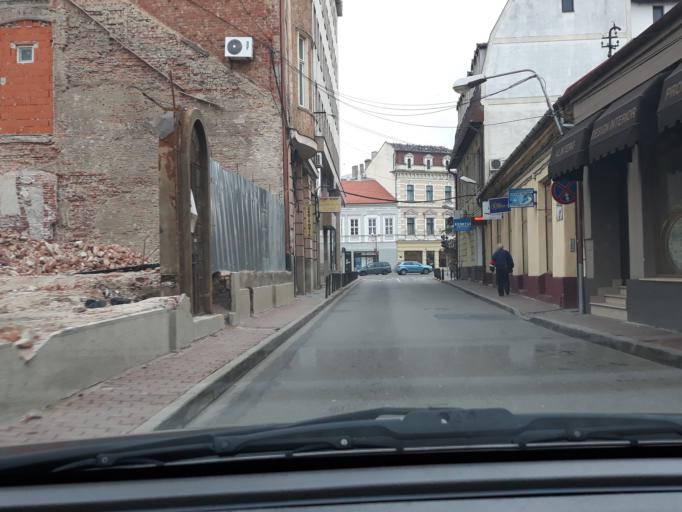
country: RO
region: Bihor
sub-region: Comuna Biharea
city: Oradea
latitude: 47.0570
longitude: 21.9289
